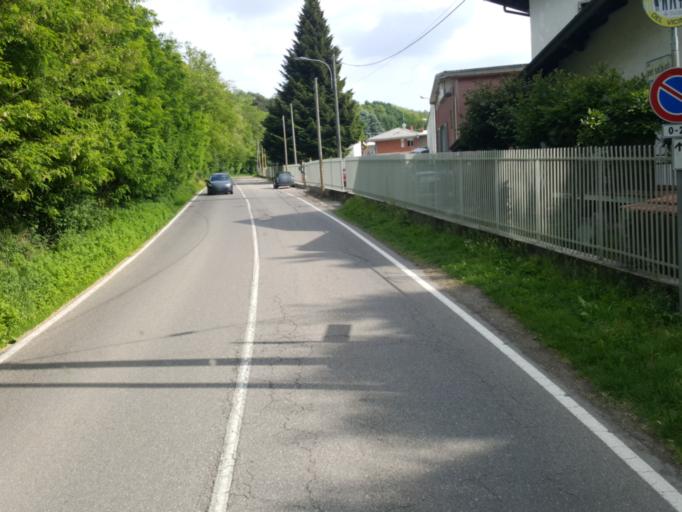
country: IT
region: Lombardy
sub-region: Provincia di Varese
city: Oggiona-Santo Stefano
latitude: 45.7101
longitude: 8.8115
